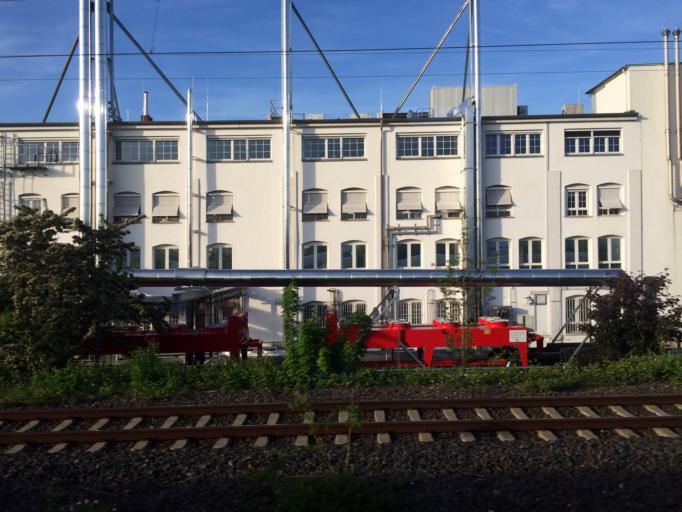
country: DE
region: Hesse
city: Niederrad
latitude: 50.0986
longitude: 8.6314
